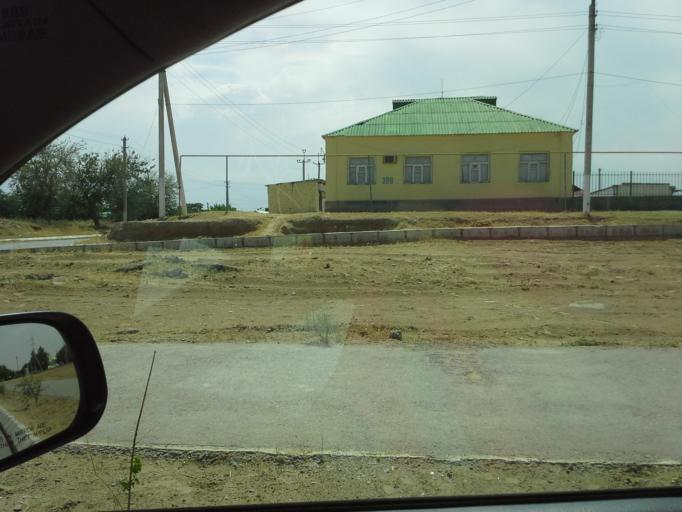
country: TM
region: Ahal
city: Ashgabat
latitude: 38.0013
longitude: 58.4059
